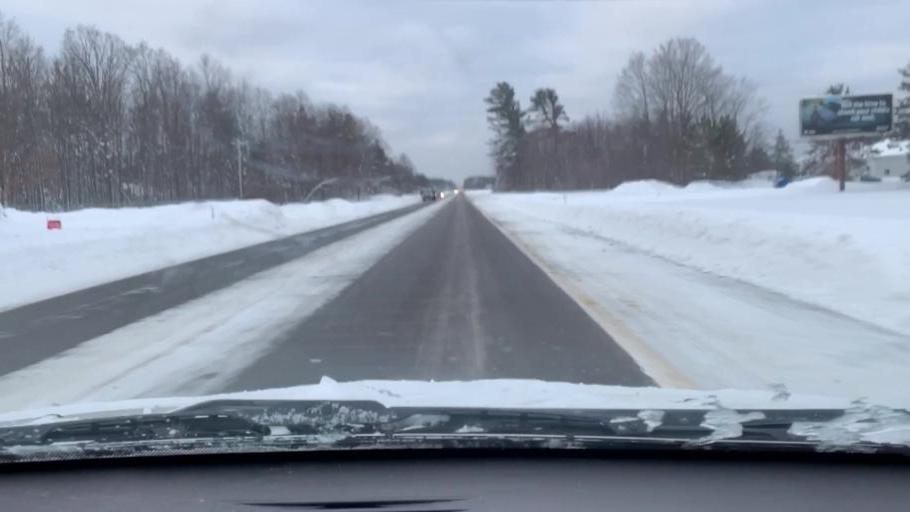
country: US
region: Michigan
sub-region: Antrim County
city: Mancelona
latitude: 44.8353
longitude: -85.1299
